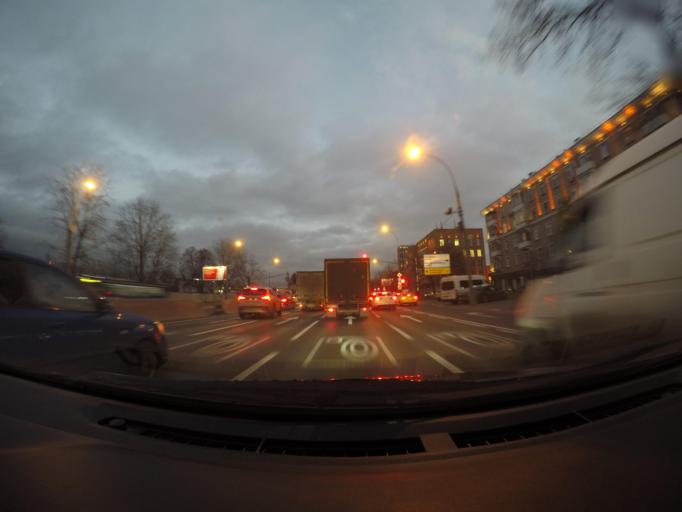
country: RU
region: Moscow
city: Kolomenskoye
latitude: 55.6450
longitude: 37.6732
